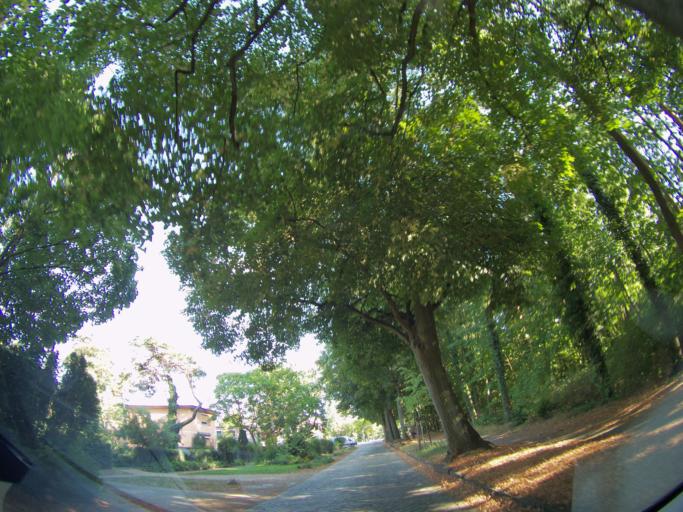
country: DE
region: Brandenburg
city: Stahnsdorf
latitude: 52.3857
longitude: 13.1922
